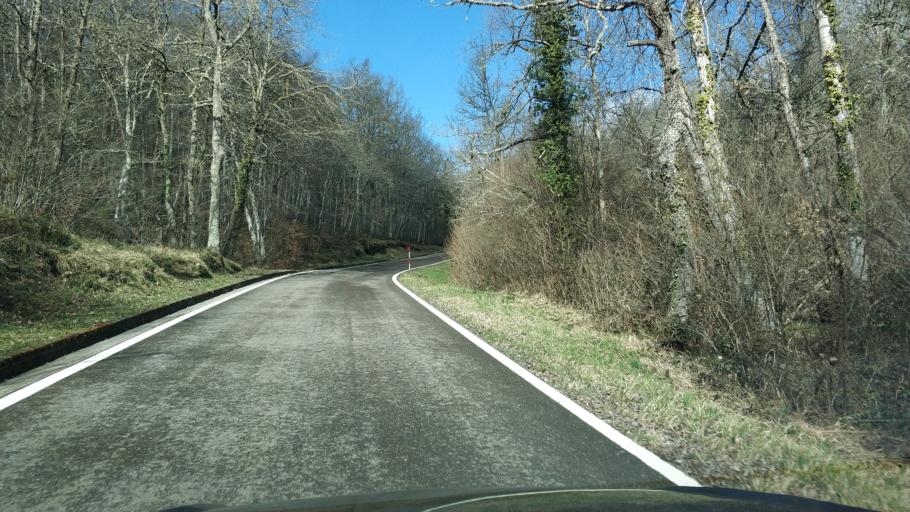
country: ES
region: Cantabria
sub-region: Provincia de Cantabria
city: Mataporquera
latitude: 42.9024
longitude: -4.0510
